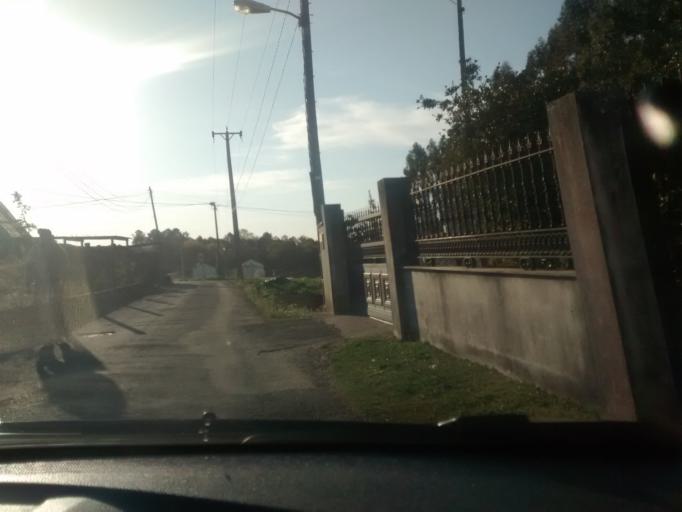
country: ES
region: Galicia
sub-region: Provincia de Pontevedra
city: A Estrada
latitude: 42.6941
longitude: -8.4848
